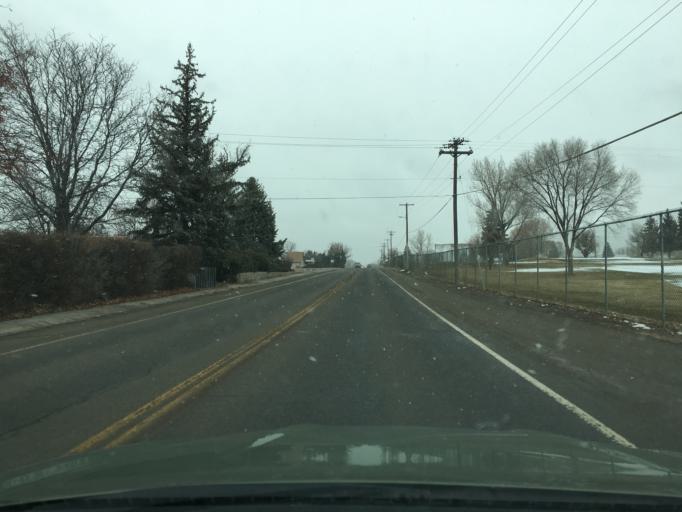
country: US
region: Colorado
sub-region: Montrose County
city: Montrose
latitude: 38.4762
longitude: -107.8566
